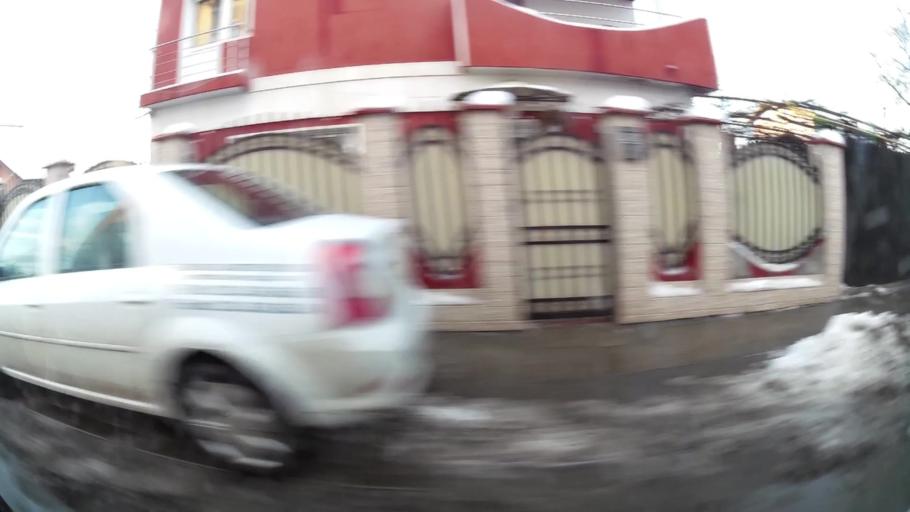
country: RO
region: Ilfov
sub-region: Comuna Popesti-Leordeni
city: Popesti-Leordeni
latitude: 44.3763
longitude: 26.1457
